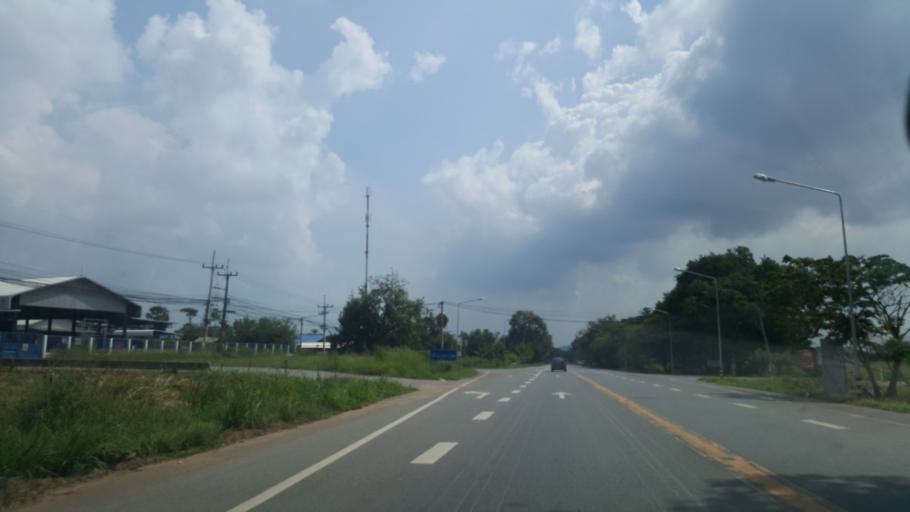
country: TH
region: Rayong
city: Ban Chang
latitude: 12.7272
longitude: 100.9691
